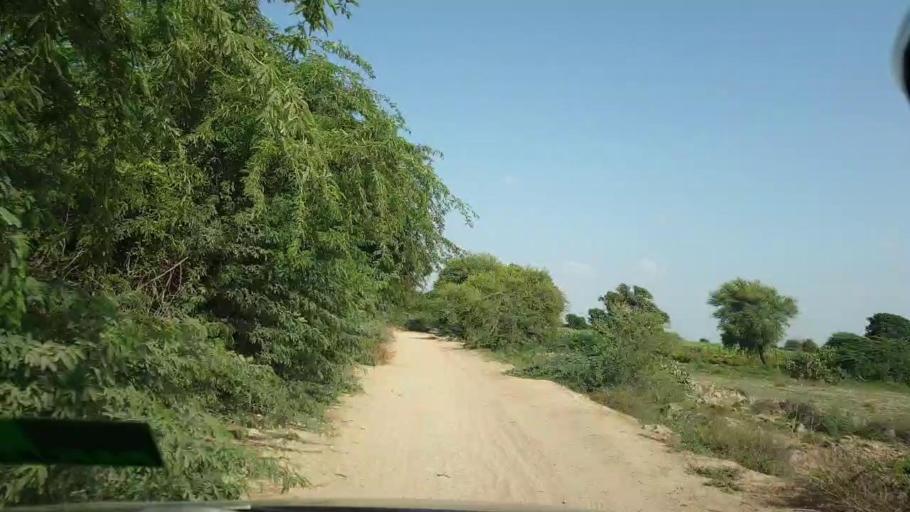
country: PK
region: Sindh
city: Naukot
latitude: 24.7030
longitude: 69.2162
